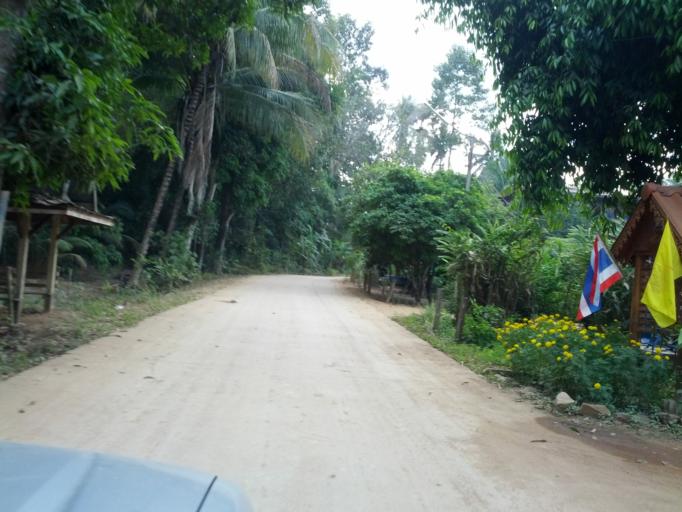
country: TH
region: Sukhothai
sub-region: Amphoe Si Satchanalai
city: Si Satchanalai
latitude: 17.4346
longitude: 99.6865
